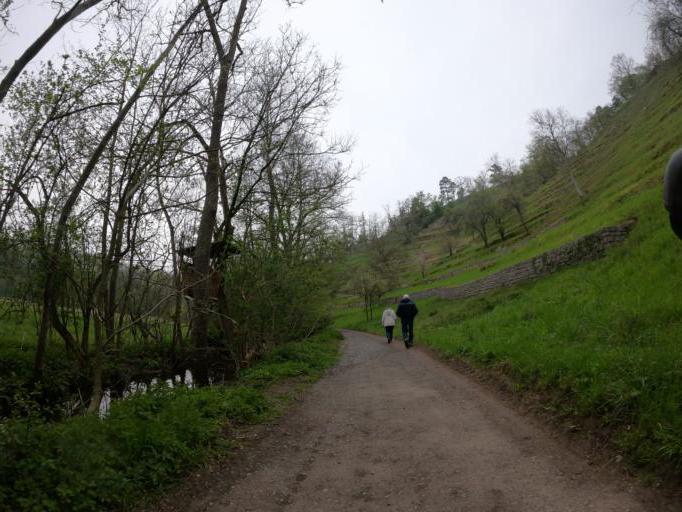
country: DE
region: Baden-Wuerttemberg
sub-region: Regierungsbezirk Stuttgart
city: Markgroningen
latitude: 48.9138
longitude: 9.0867
